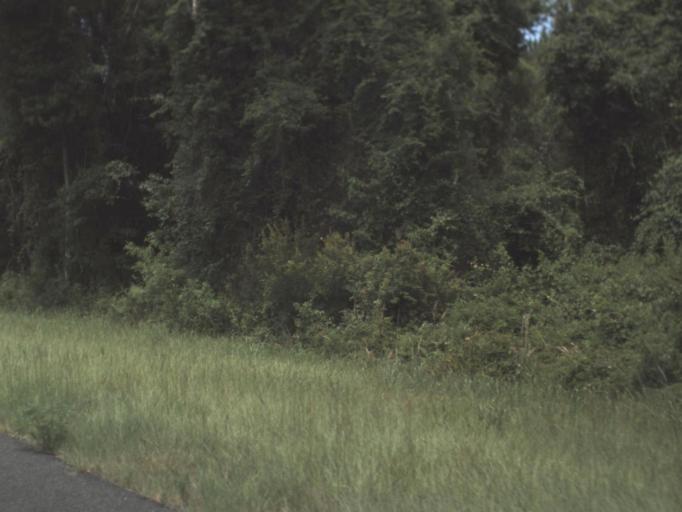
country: US
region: Florida
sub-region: Taylor County
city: Perry
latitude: 30.2068
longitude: -83.6606
